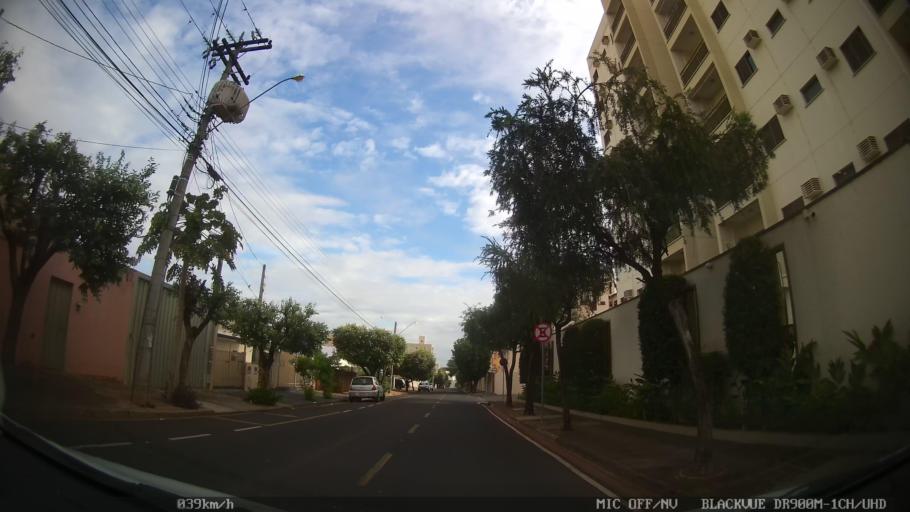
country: BR
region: Sao Paulo
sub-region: Sao Jose Do Rio Preto
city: Sao Jose do Rio Preto
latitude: -20.8323
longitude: -49.3827
